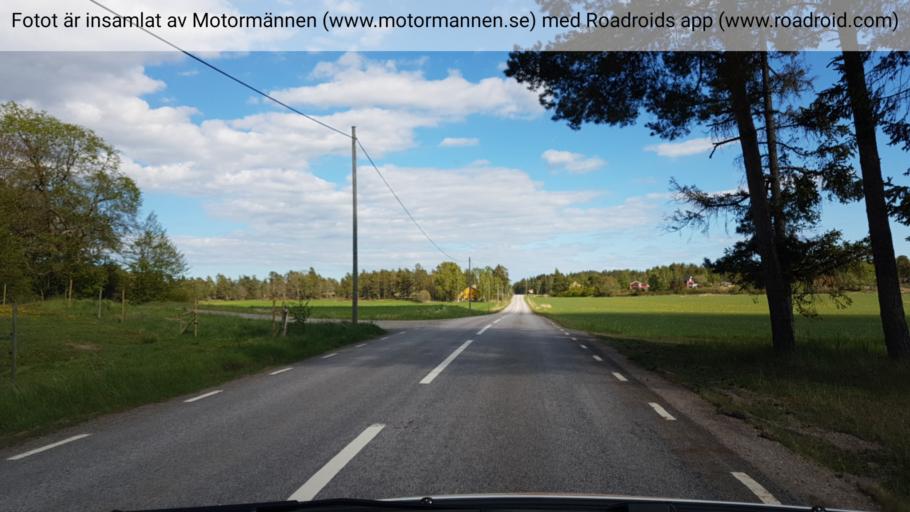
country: SE
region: Kalmar
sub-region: Vasterviks Kommun
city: Forserum
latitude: 57.9313
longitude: 16.5158
